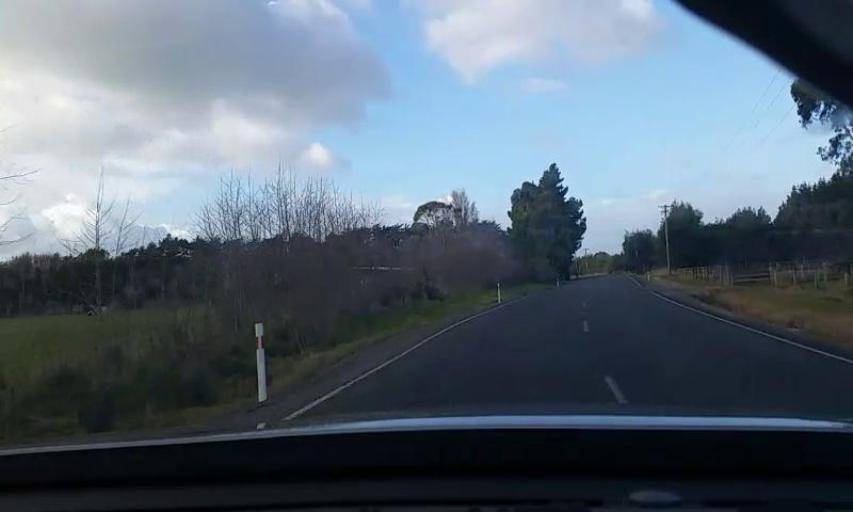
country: NZ
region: Southland
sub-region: Invercargill City
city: Invercargill
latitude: -46.3807
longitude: 168.4374
